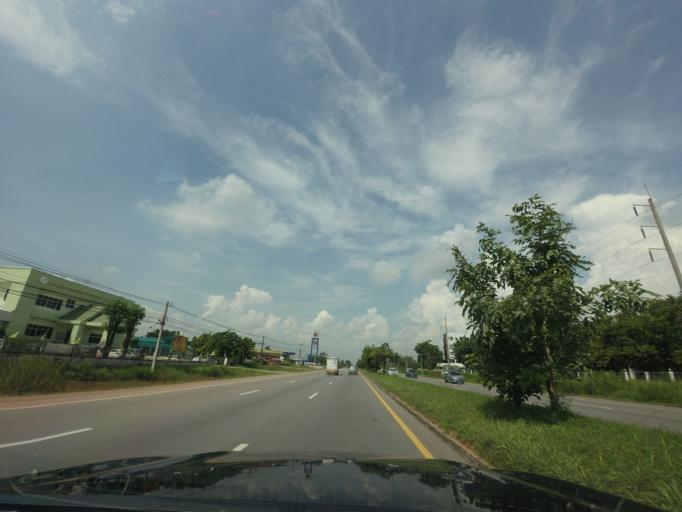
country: TH
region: Khon Kaen
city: Khon Kaen
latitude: 16.4506
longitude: 102.7403
